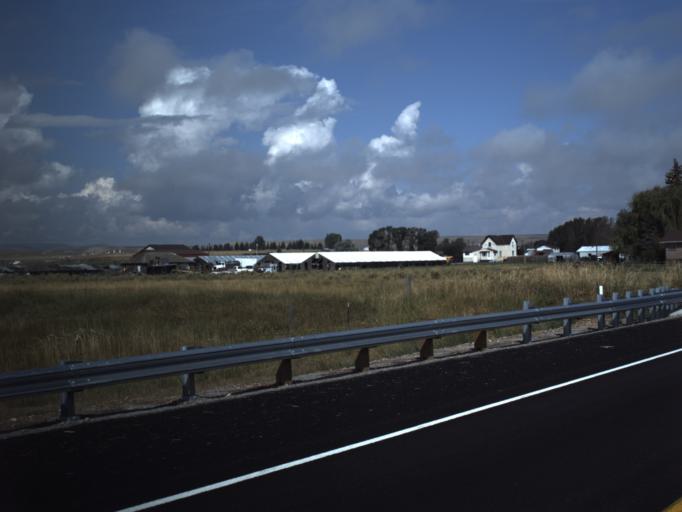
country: US
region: Utah
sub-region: Rich County
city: Randolph
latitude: 41.6572
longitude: -111.1849
